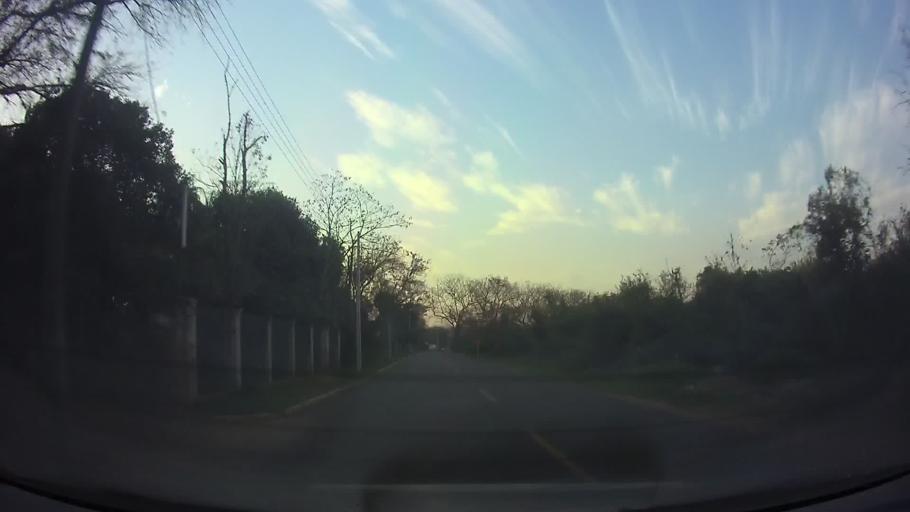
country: PY
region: Central
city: Limpio
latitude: -25.2416
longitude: -57.4948
